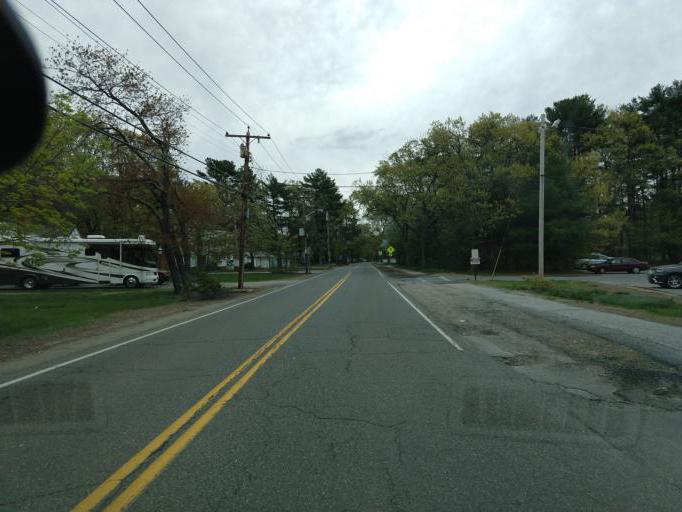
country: US
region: Massachusetts
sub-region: Middlesex County
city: Tewksbury
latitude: 42.5842
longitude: -71.2183
